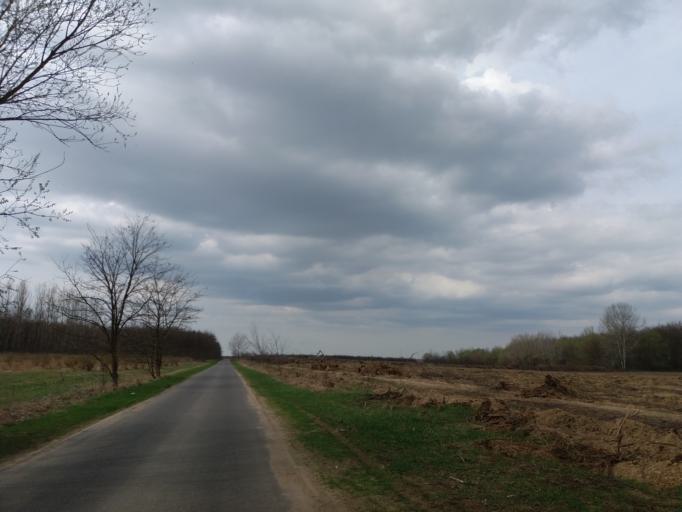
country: HU
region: Szabolcs-Szatmar-Bereg
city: Nyirtass
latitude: 48.0870
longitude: 22.0363
